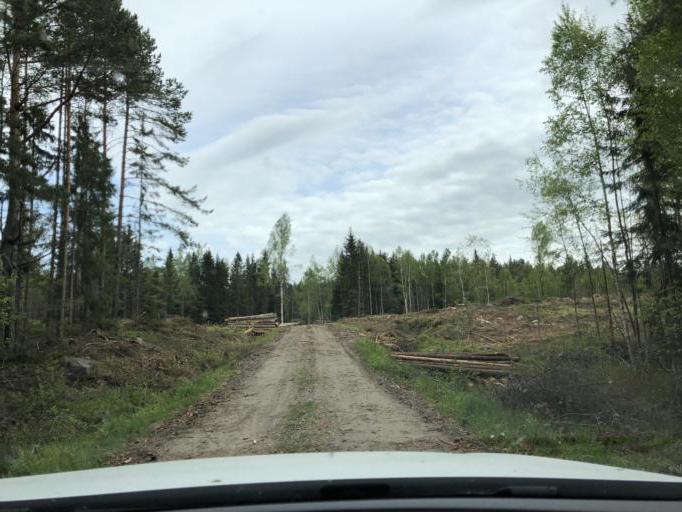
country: SE
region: Uppsala
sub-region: Heby Kommun
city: OEstervala
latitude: 60.3749
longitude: 17.2302
